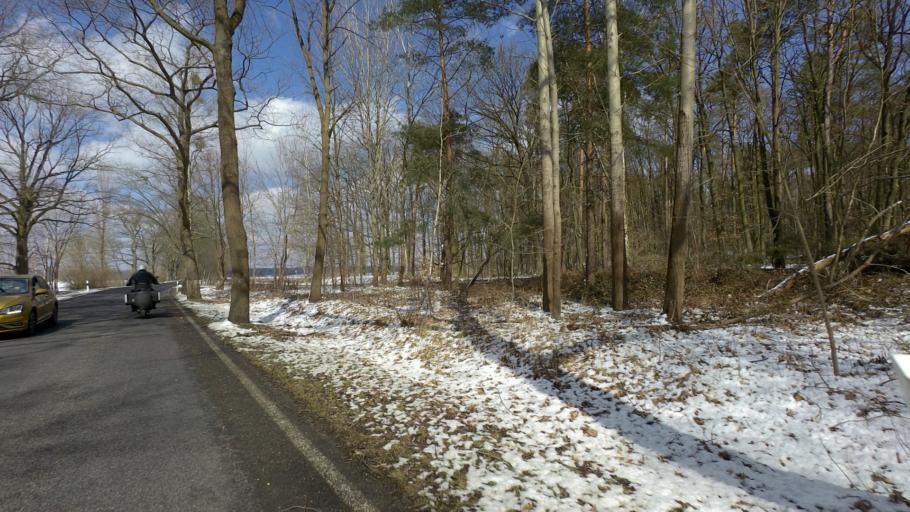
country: DE
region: Brandenburg
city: Joachimsthal
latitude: 52.8962
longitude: 13.7155
